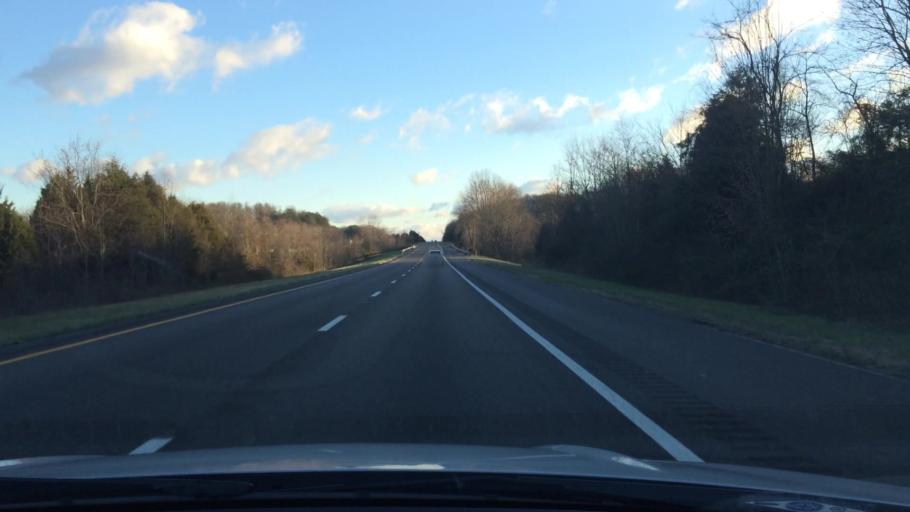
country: US
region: Tennessee
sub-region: Washington County
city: Fall Branch
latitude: 36.3861
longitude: -82.6614
